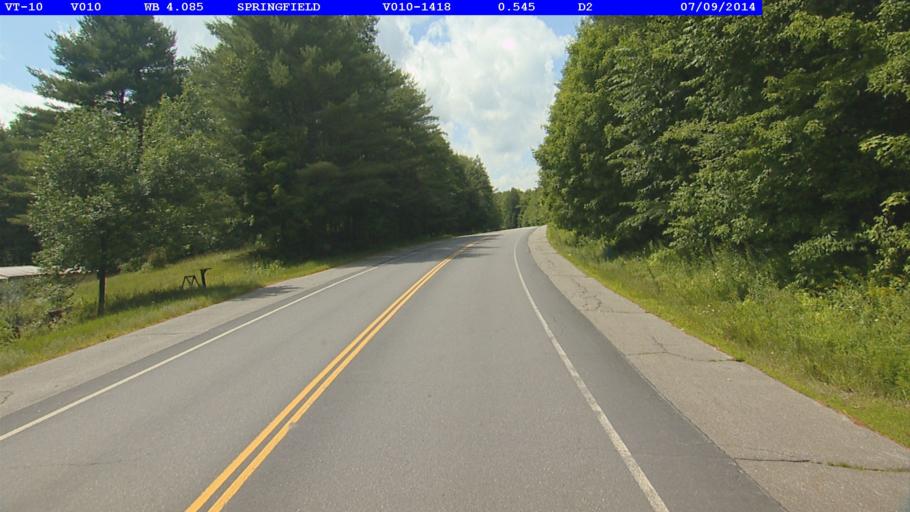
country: US
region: Vermont
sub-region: Windsor County
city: Springfield
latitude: 43.3363
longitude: -72.5365
